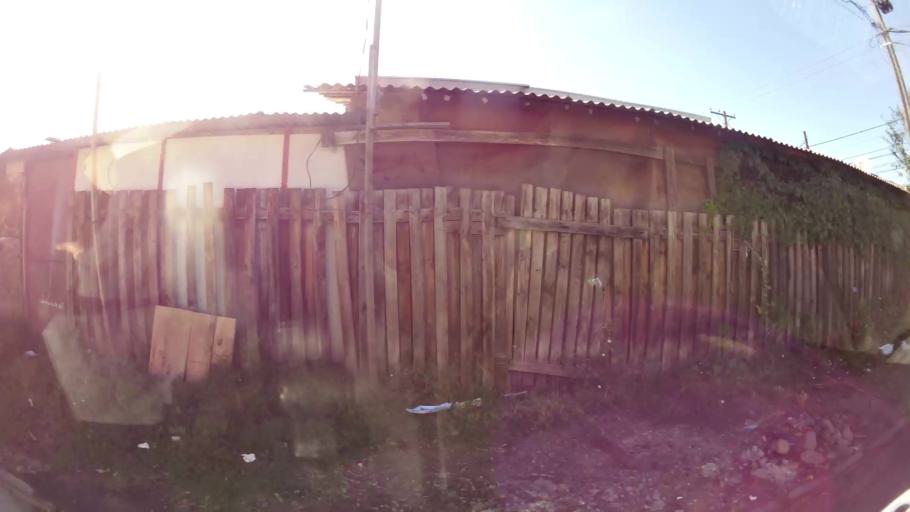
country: CL
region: Maule
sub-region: Provincia de Curico
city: Curico
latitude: -34.9917
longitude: -71.2562
